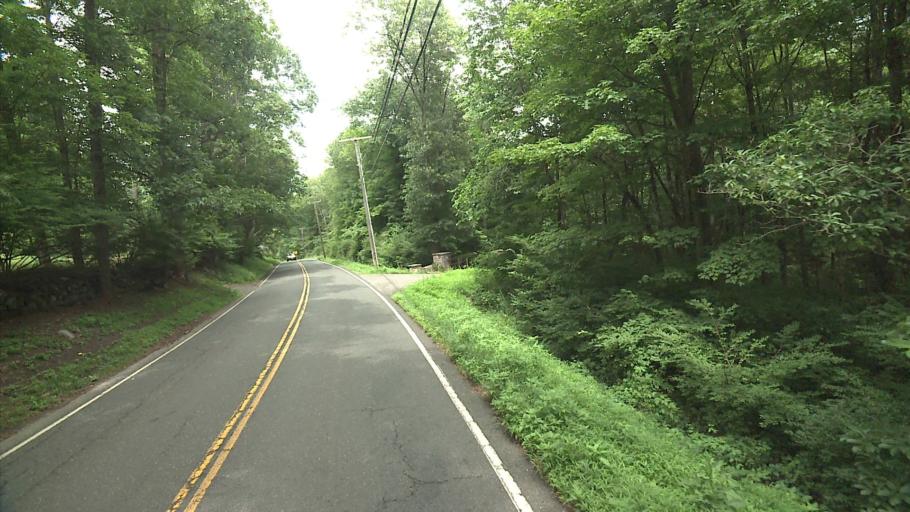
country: US
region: Connecticut
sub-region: Litchfield County
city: New Milford
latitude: 41.5523
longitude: -73.3287
